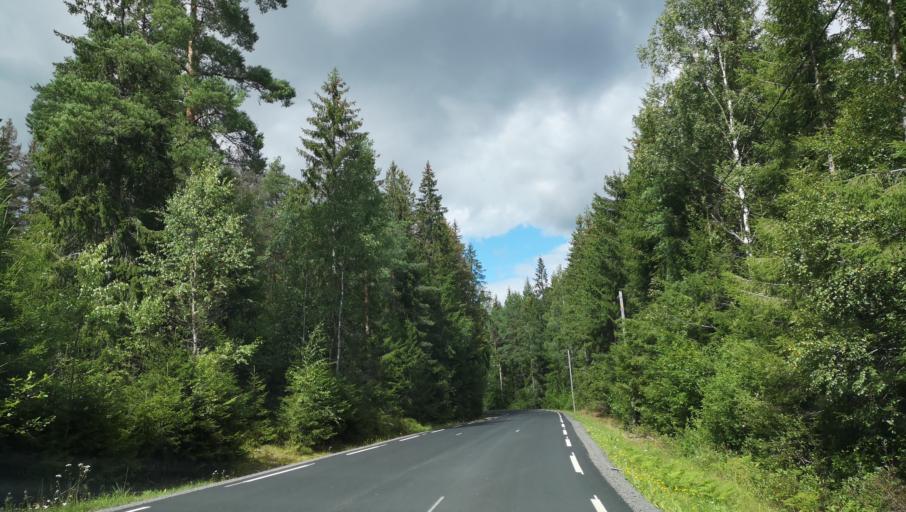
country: NO
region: Ostfold
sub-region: Hobol
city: Elvestad
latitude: 59.6810
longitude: 10.9408
